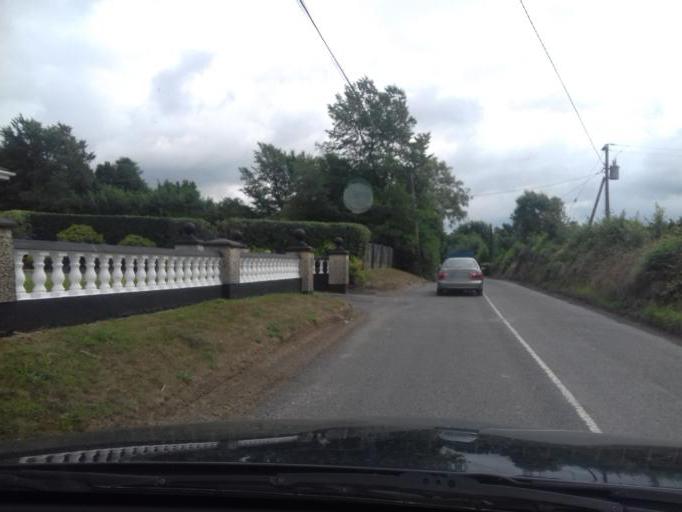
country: IE
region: Leinster
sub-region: Loch Garman
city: Ballinroad
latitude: 52.4831
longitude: -6.4325
